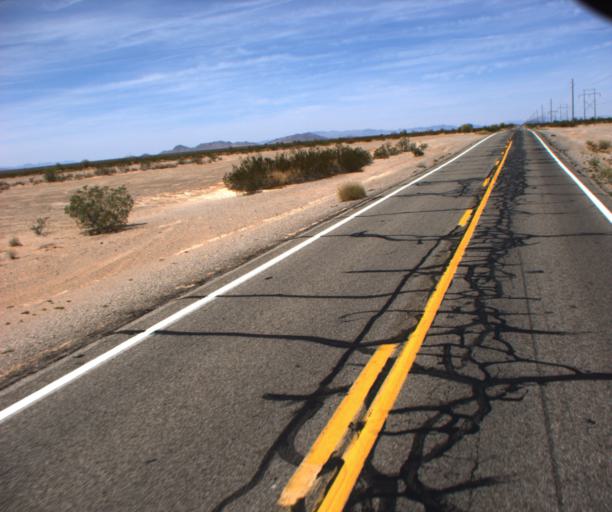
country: US
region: Arizona
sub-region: La Paz County
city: Quartzsite
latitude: 33.8303
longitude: -114.2170
